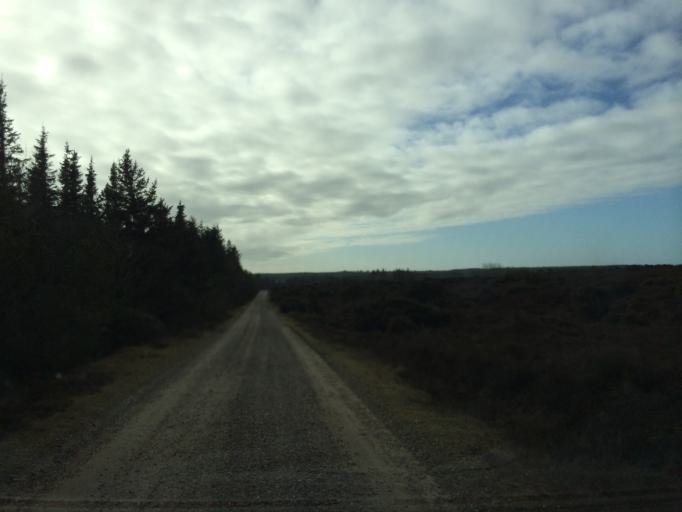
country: DK
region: Central Jutland
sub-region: Holstebro Kommune
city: Ulfborg
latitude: 56.2546
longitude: 8.4247
